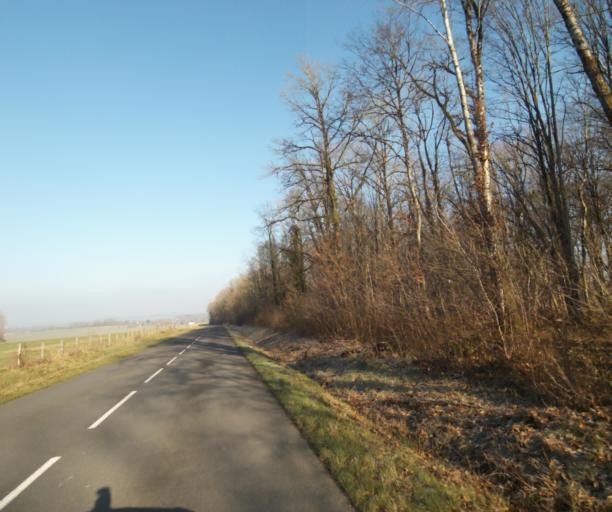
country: FR
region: Champagne-Ardenne
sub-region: Departement de la Haute-Marne
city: Wassy
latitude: 48.4822
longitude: 4.9349
